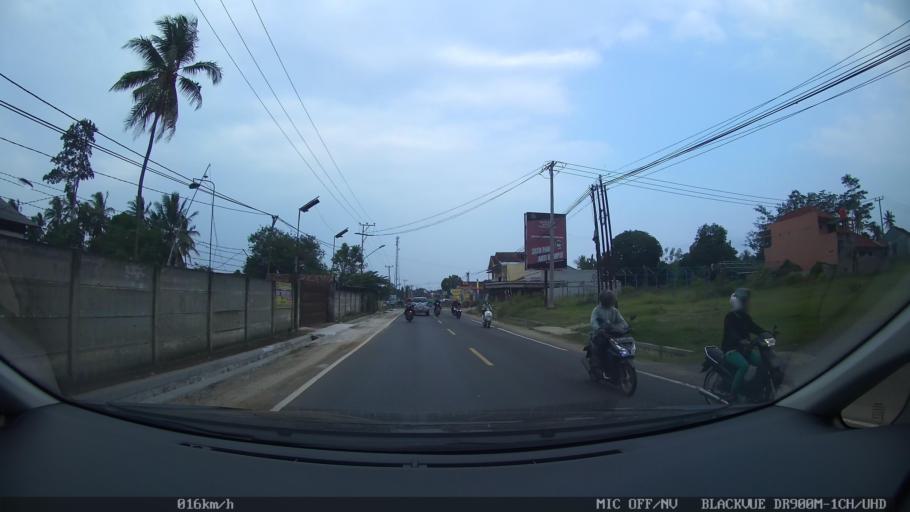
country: ID
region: Lampung
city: Gedongtataan
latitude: -5.3660
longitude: 105.1452
